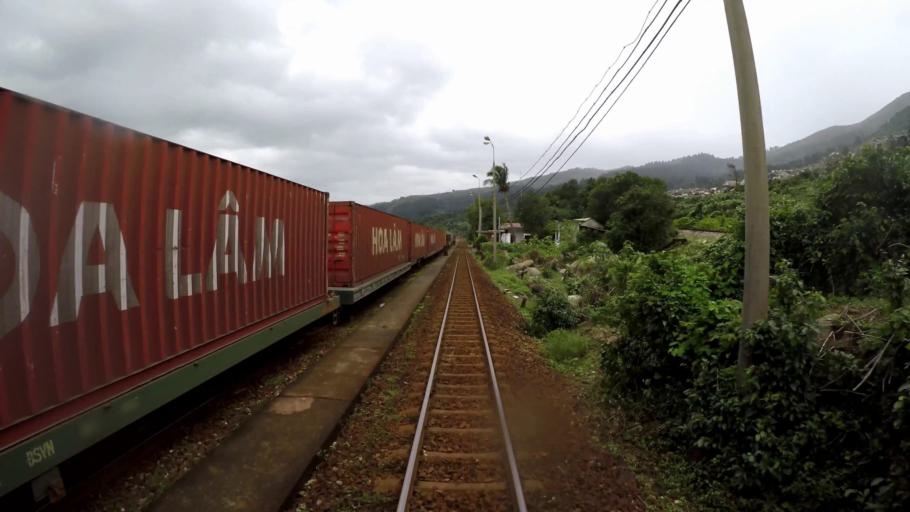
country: VN
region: Da Nang
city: Lien Chieu
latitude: 16.1676
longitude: 108.1359
